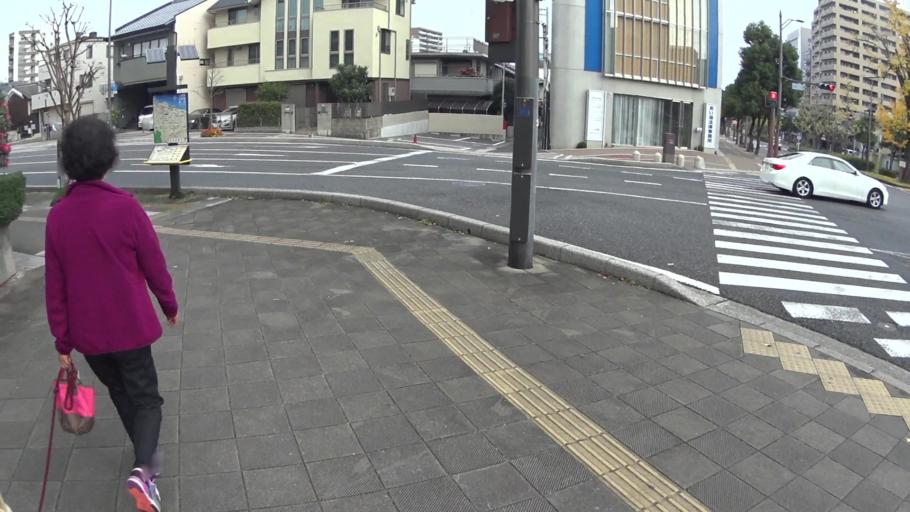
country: JP
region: Shiga Prefecture
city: Otsu-shi
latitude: 35.0060
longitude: 135.8655
